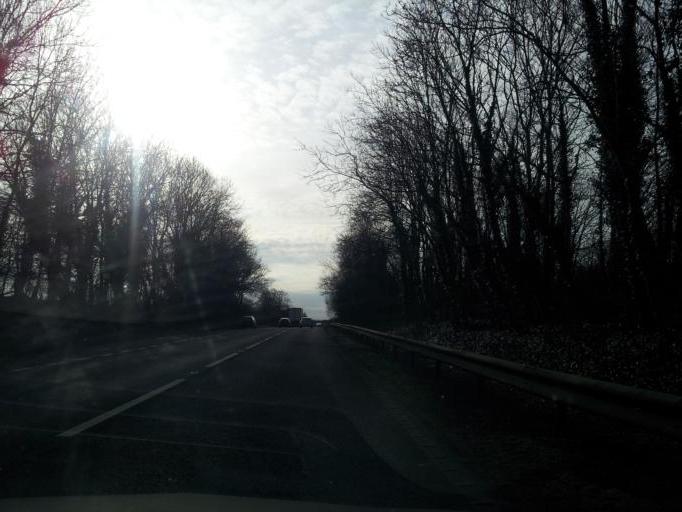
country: GB
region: England
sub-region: Peterborough
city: Castor
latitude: 52.5497
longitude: -0.3364
